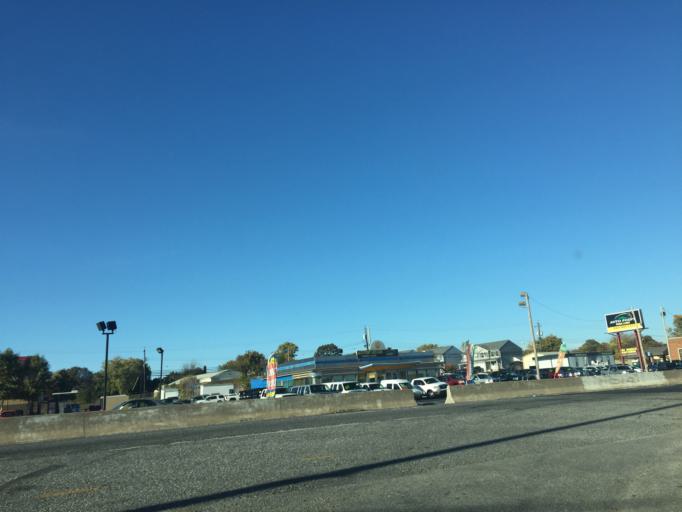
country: US
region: Maryland
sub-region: Baltimore County
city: Rosedale
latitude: 39.3231
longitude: -76.5025
